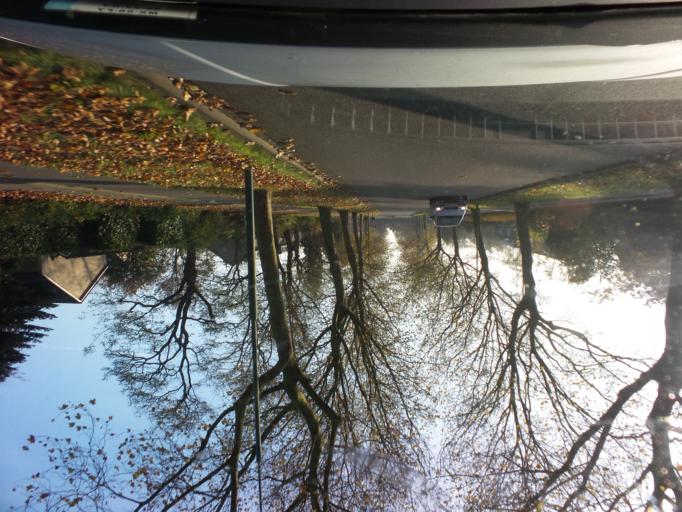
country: NL
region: Utrecht
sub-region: Gemeente Leusden
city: Leusden
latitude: 52.1339
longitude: 5.4232
